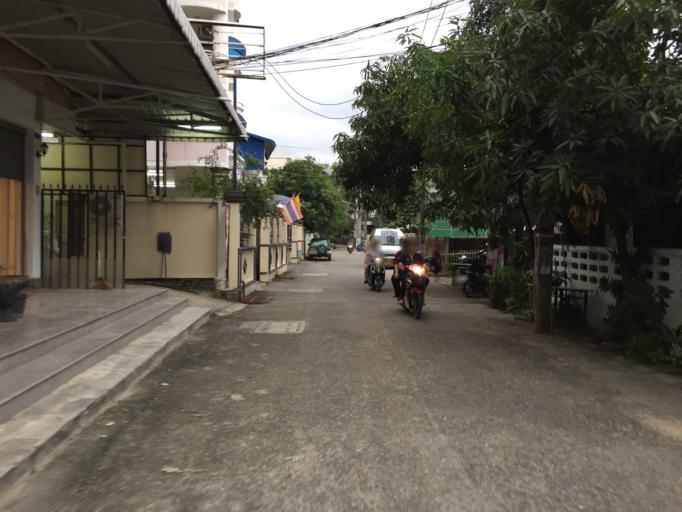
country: TH
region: Chiang Mai
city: Chiang Mai
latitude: 18.8009
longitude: 98.9624
